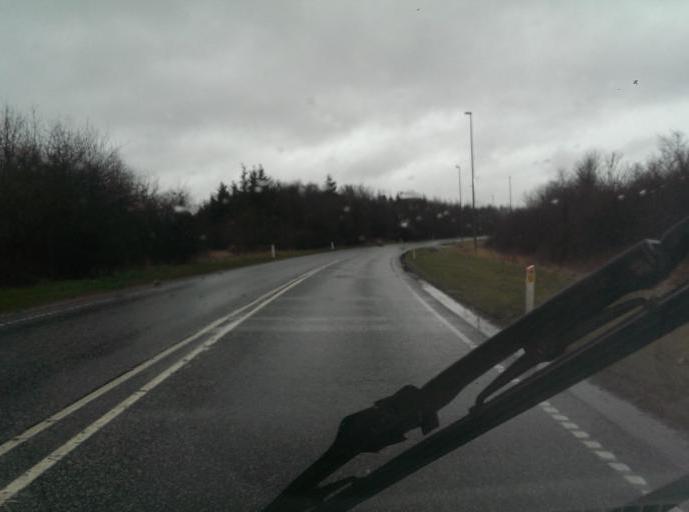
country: DK
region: Central Jutland
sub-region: Ringkobing-Skjern Kommune
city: Tarm
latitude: 55.9134
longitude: 8.5081
